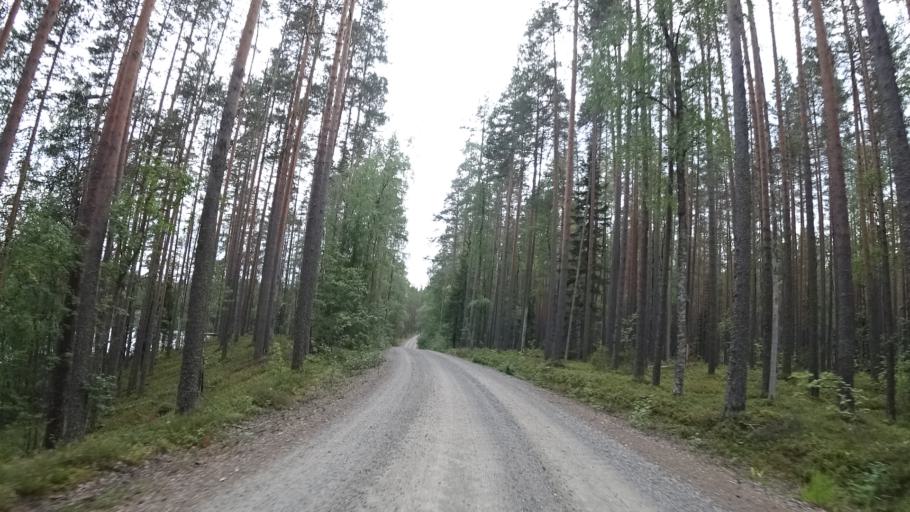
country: FI
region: North Karelia
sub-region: Joensuu
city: Ilomantsi
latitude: 62.5980
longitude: 31.1844
